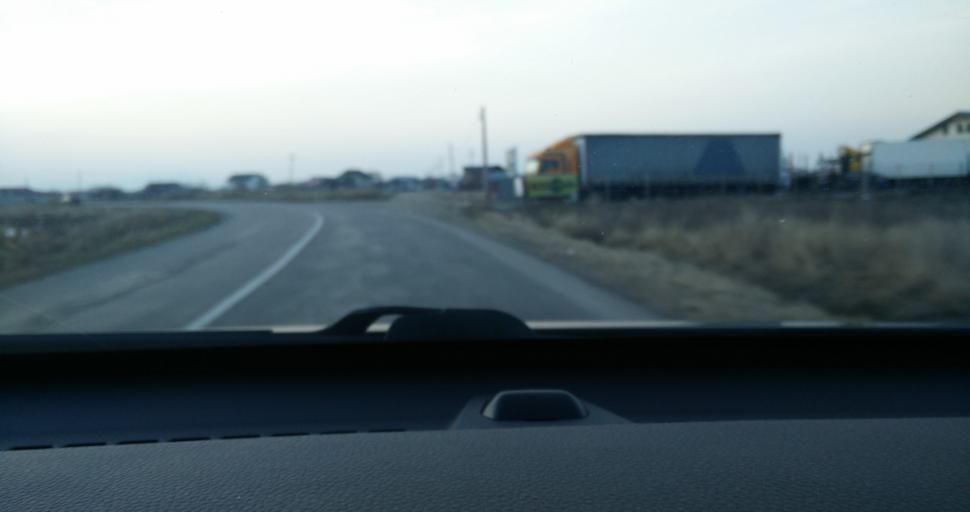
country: RO
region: Vrancea
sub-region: Comuna Milcovul
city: Milcovul
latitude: 45.6763
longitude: 27.2520
